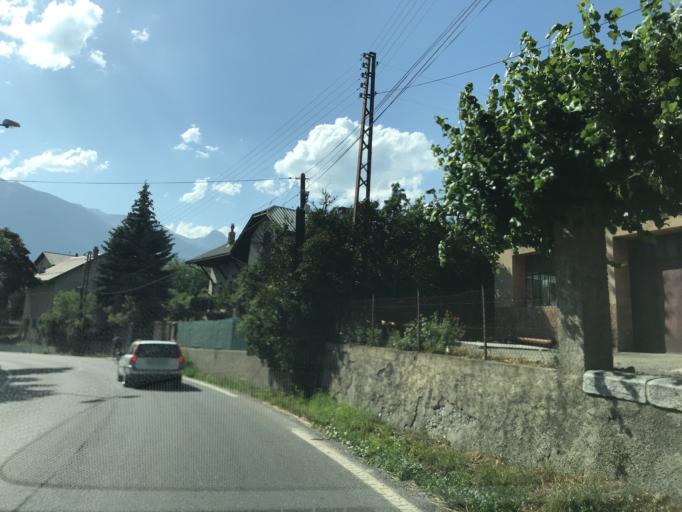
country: FR
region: Provence-Alpes-Cote d'Azur
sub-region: Departement des Hautes-Alpes
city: Guillestre
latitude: 44.6598
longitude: 6.6410
